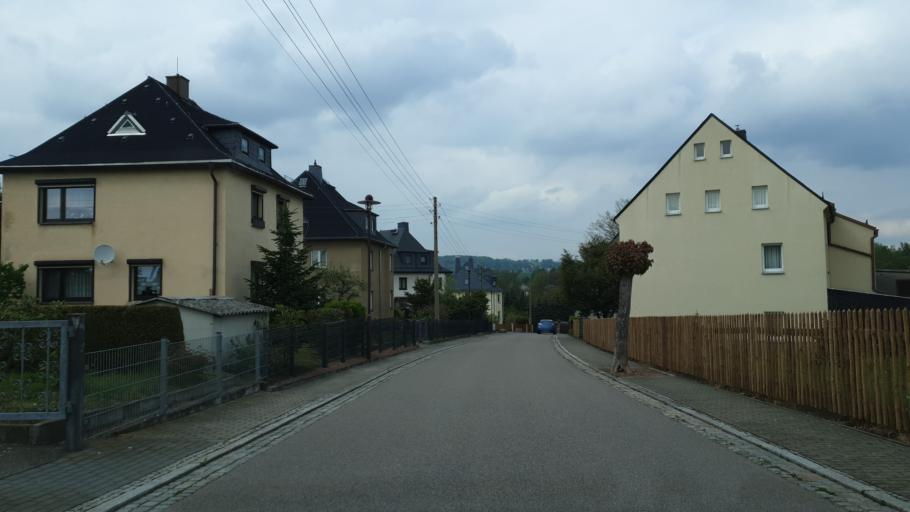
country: DE
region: Saxony
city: Oberlungwitz
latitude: 50.7782
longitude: 12.7096
